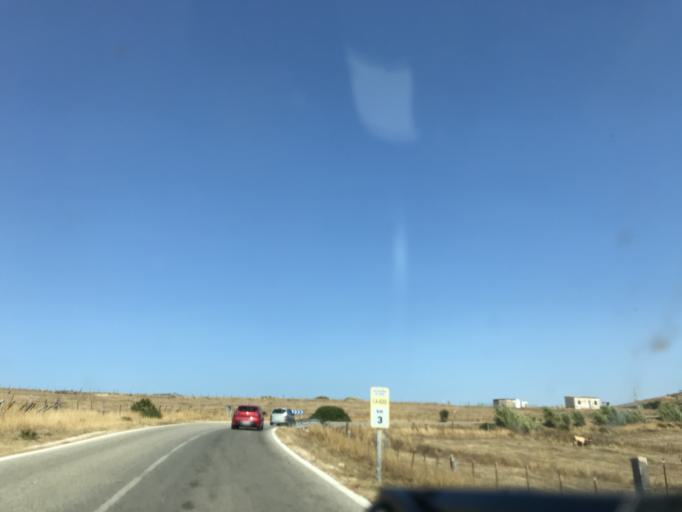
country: ES
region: Andalusia
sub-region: Provincia de Cadiz
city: Zahara de los Atunes
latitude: 36.1022
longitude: -5.7350
